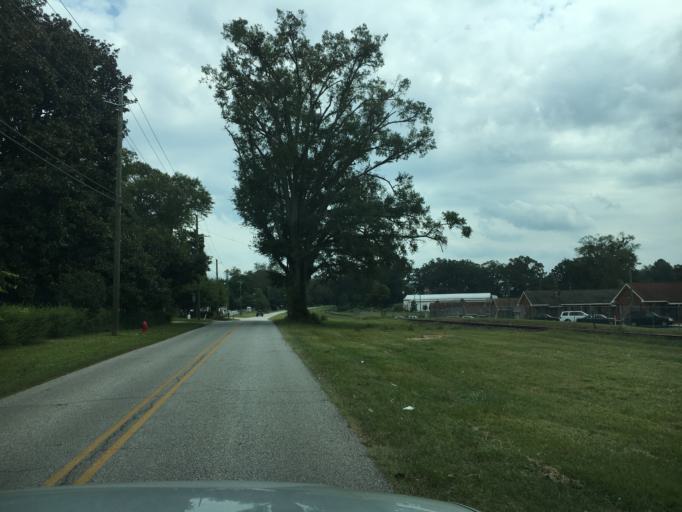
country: US
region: Georgia
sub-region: Franklin County
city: Lavonia
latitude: 34.4415
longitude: -83.1105
